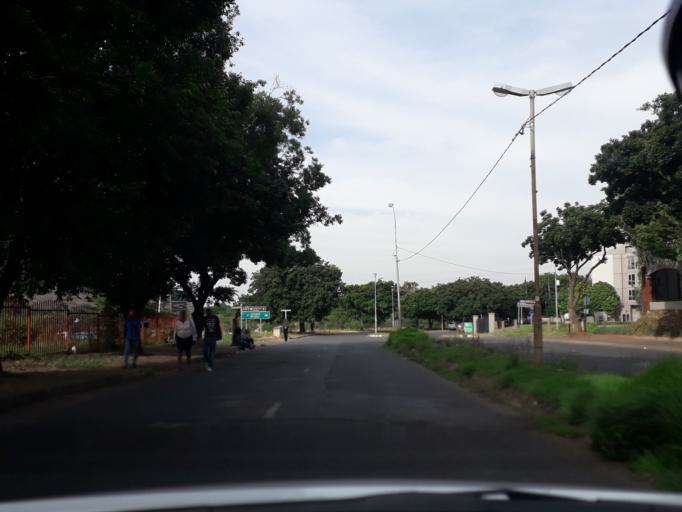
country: ZA
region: Gauteng
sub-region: City of Johannesburg Metropolitan Municipality
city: Johannesburg
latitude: -26.1785
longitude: 28.1121
